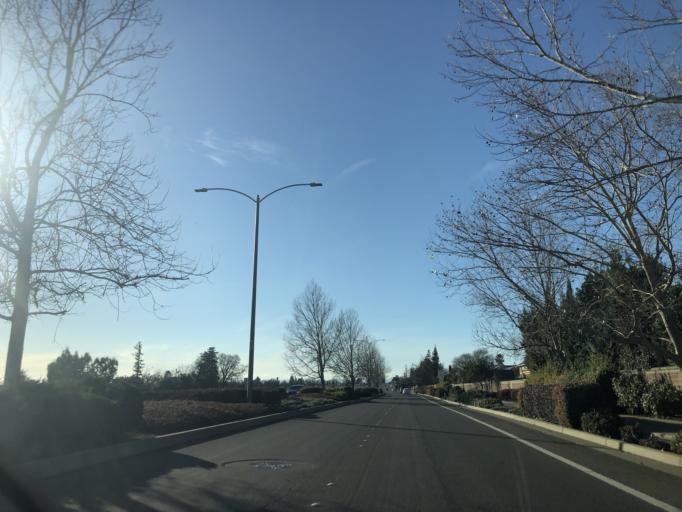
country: US
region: California
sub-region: Yolo County
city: Woodland
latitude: 38.6628
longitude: -121.7438
